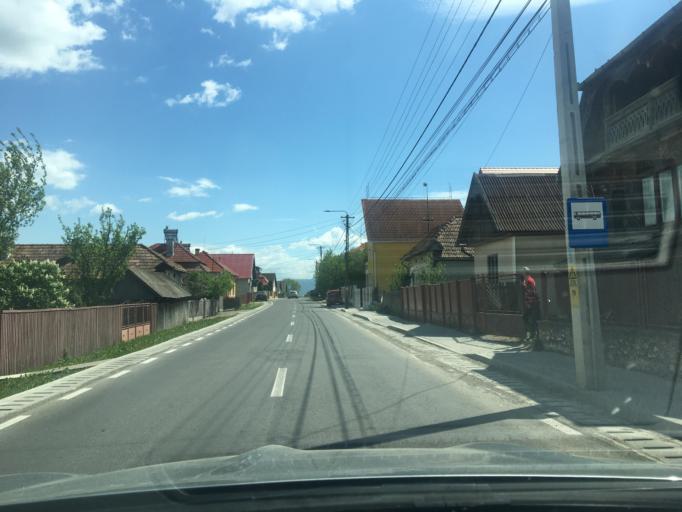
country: RO
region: Harghita
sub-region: Comuna Remetea
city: Remetea
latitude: 46.8081
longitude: 25.4597
